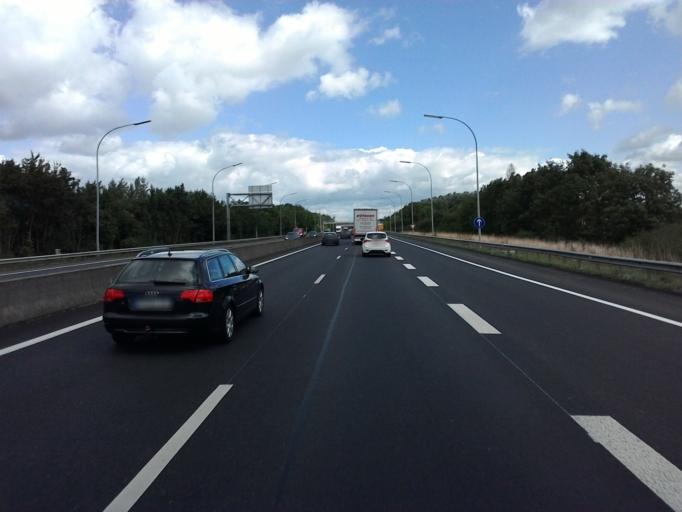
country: LU
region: Luxembourg
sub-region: Canton de Luxembourg
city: Strassen
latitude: 49.6082
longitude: 6.0815
